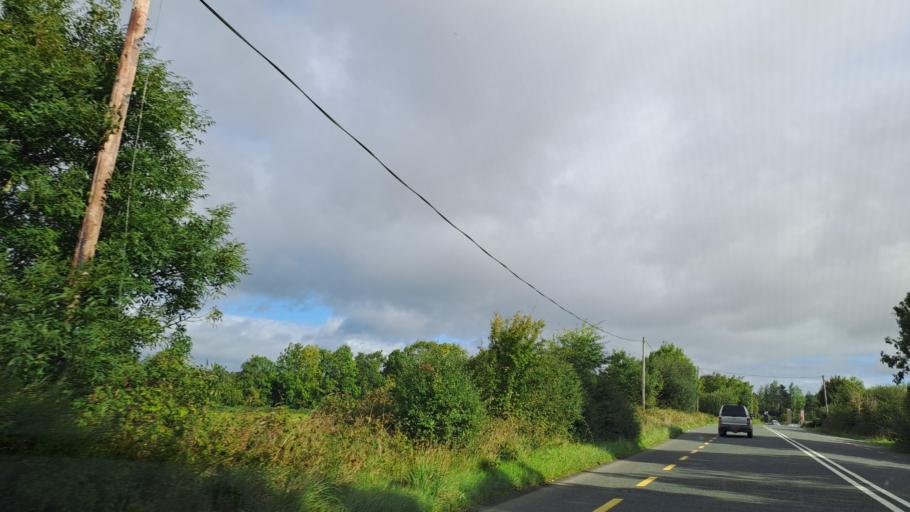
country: IE
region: Ulster
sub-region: County Monaghan
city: Carrickmacross
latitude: 53.9482
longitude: -6.7627
